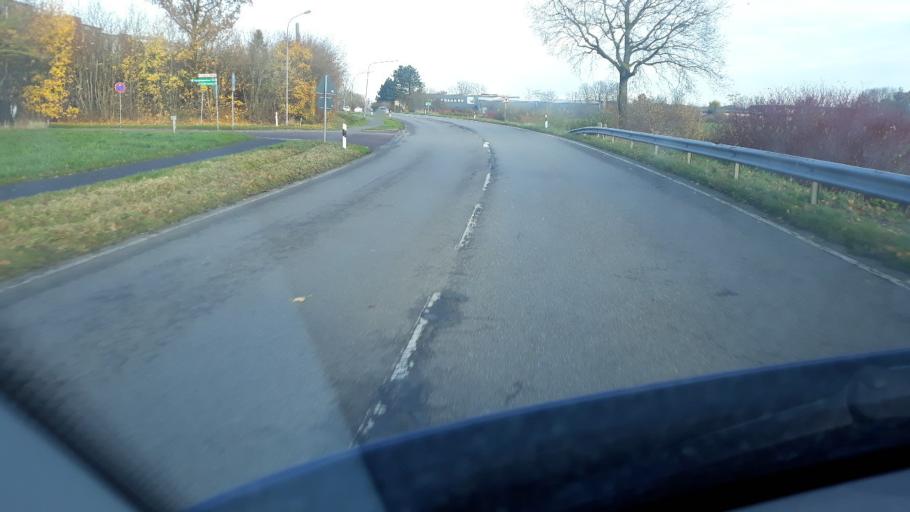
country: DE
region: Schleswig-Holstein
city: Kappeln
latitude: 54.6604
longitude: 9.9512
